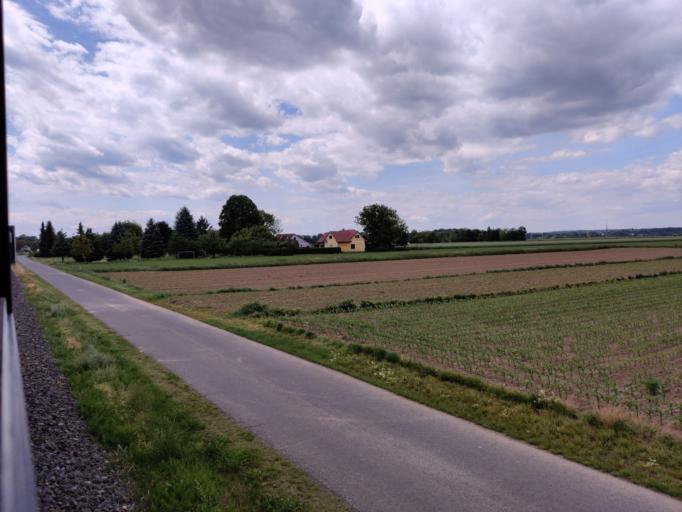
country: AT
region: Styria
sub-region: Politischer Bezirk Suedoststeiermark
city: Weinburg am Sassbach
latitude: 46.7147
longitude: 15.7260
